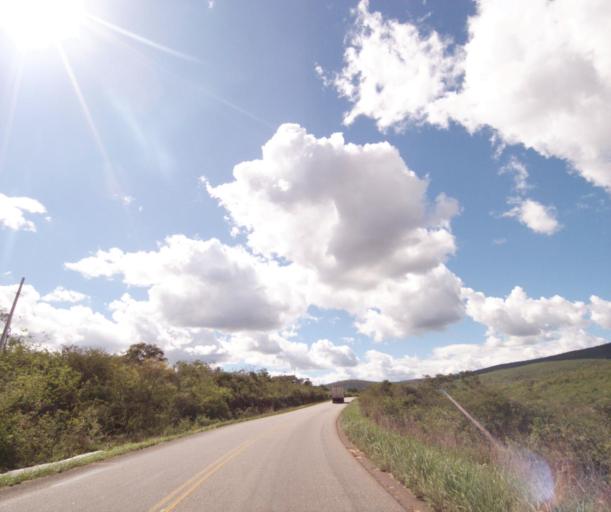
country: BR
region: Bahia
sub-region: Caetite
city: Caetite
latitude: -14.1515
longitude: -42.3548
